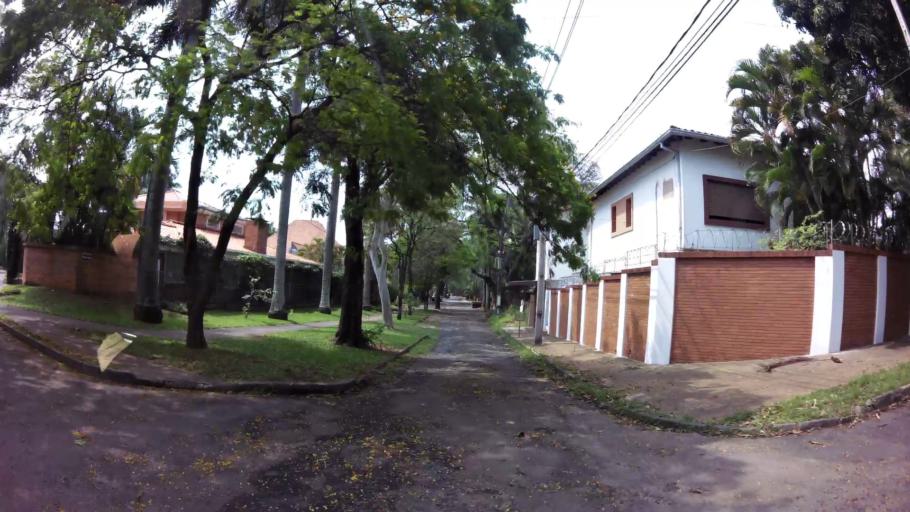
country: PY
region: Asuncion
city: Asuncion
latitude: -25.2901
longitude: -57.5999
